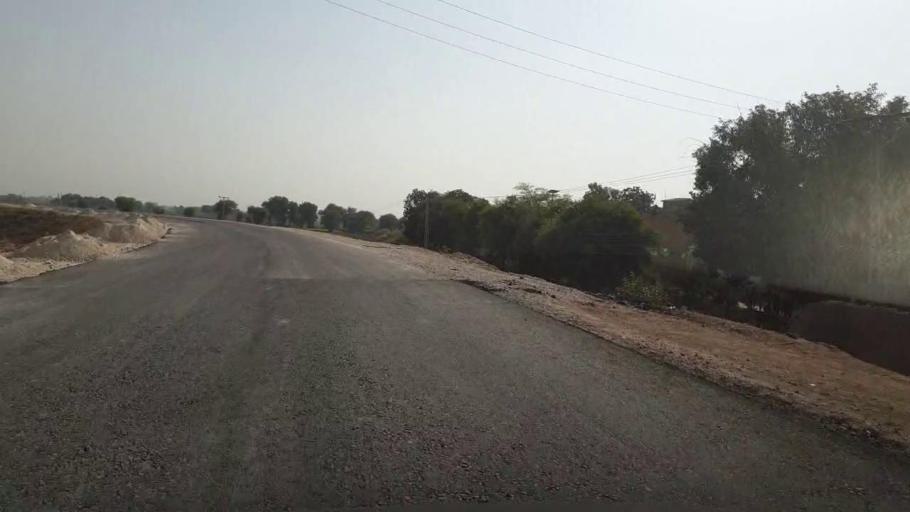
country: PK
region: Sindh
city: Bhan
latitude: 26.5618
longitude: 67.7741
